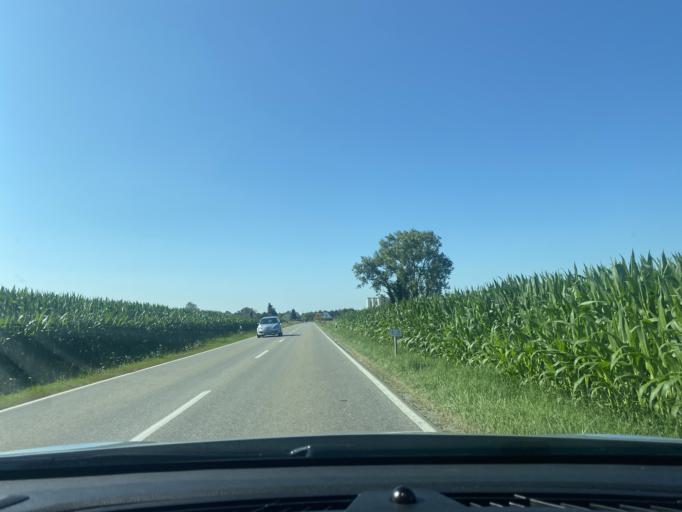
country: DE
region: Bavaria
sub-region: Upper Bavaria
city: Erding
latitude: 48.3207
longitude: 11.8936
